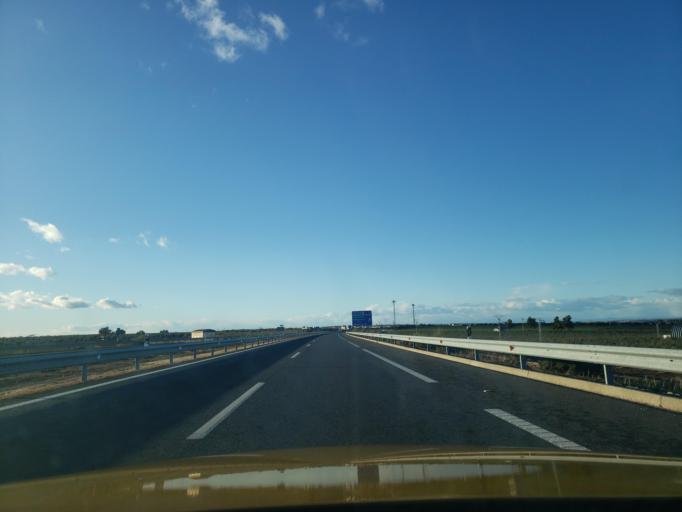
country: ES
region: Castille-La Mancha
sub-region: Province of Toledo
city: Nambroca
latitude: 39.7854
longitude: -3.9229
